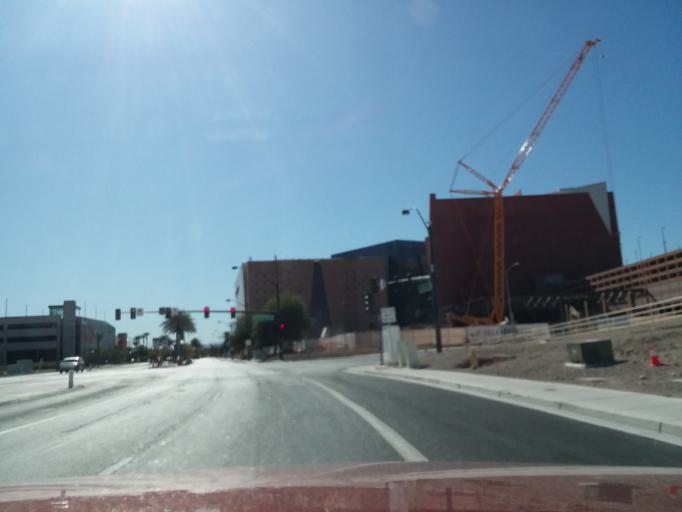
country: US
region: Nevada
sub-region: Clark County
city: Las Vegas
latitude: 36.1708
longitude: -115.1535
